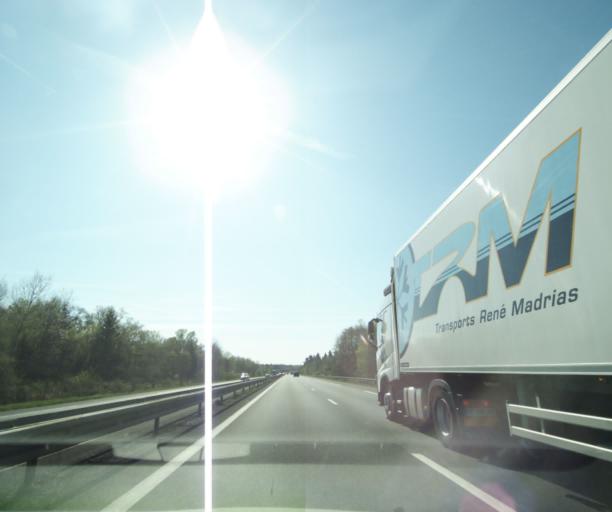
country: FR
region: Centre
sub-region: Departement du Loiret
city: La Ferte-Saint-Aubin
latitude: 47.7243
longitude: 1.8865
